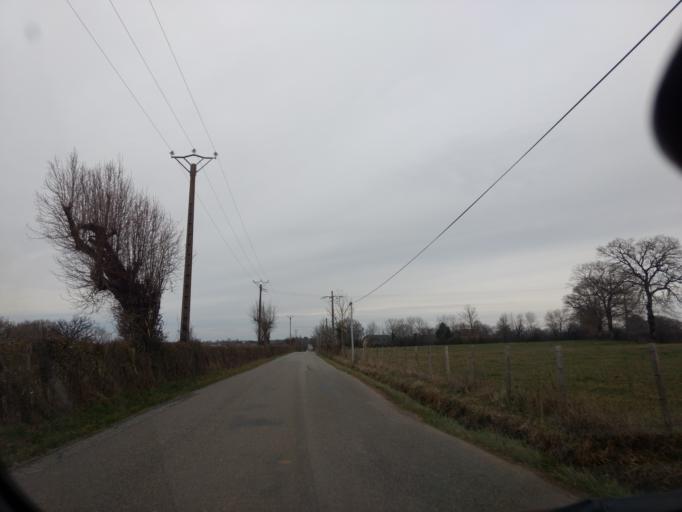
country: FR
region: Midi-Pyrenees
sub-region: Departement de l'Aveyron
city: Saint-Christophe-Vallon
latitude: 44.4358
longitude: 2.3572
